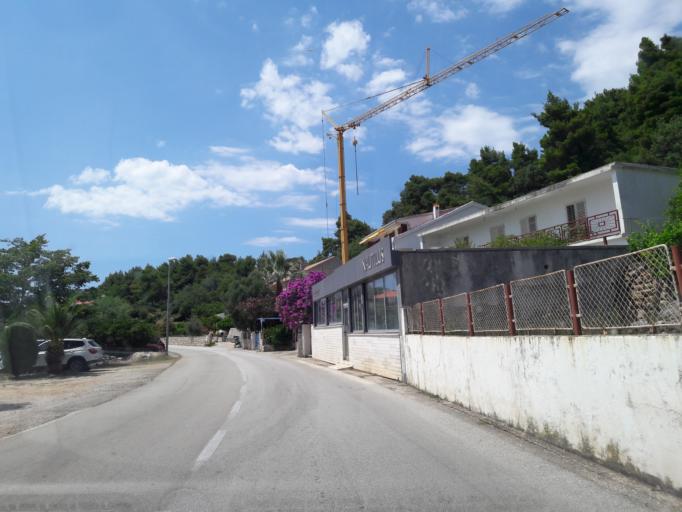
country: HR
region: Dubrovacko-Neretvanska
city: Korcula
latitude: 42.9749
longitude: 17.1457
